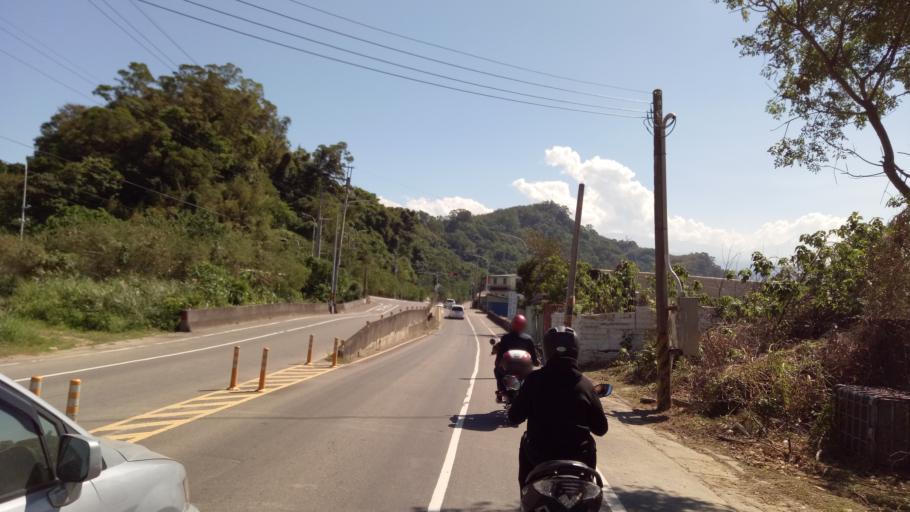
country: TW
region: Taiwan
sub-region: Hsinchu
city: Hsinchu
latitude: 24.6831
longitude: 120.9631
